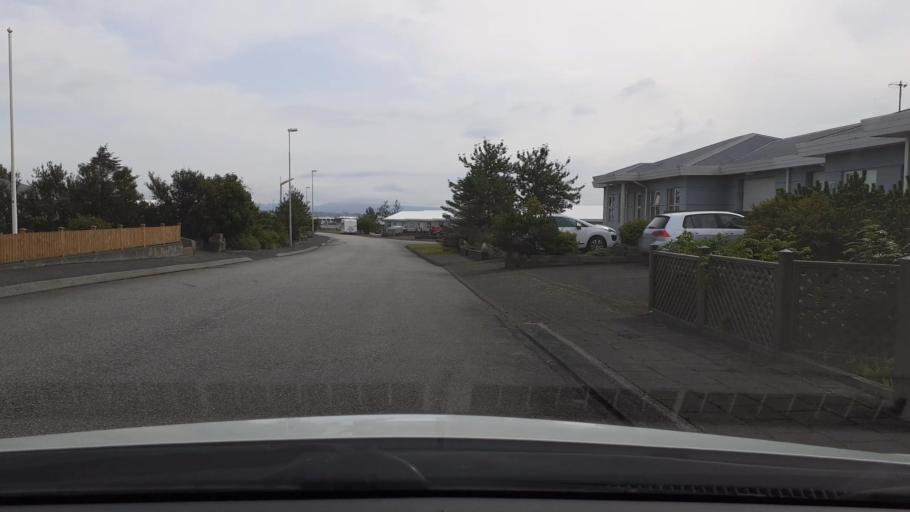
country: IS
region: Southern Peninsula
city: Reykjanesbaer
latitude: 63.9970
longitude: -22.5734
